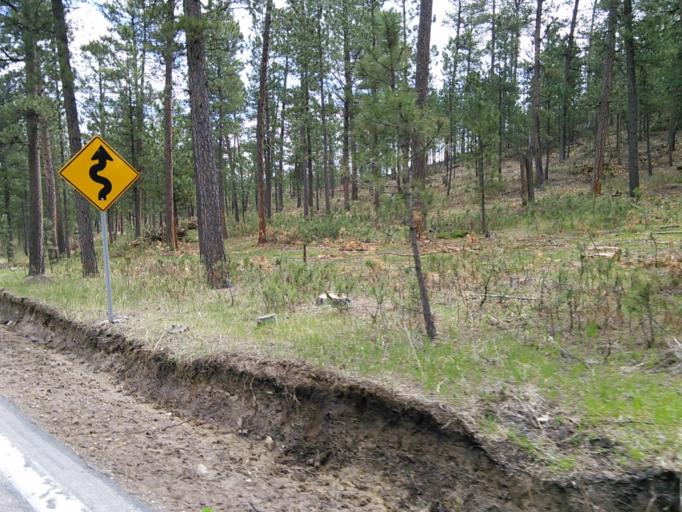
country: US
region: South Dakota
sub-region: Custer County
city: Custer
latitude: 43.7652
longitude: -103.4622
